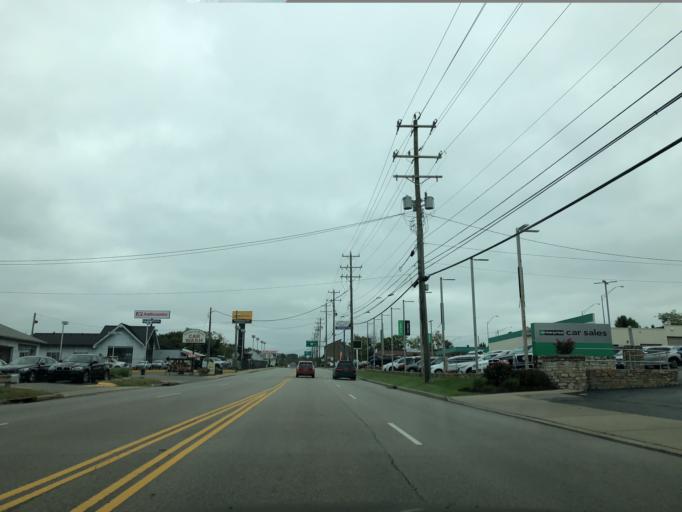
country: US
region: Ohio
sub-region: Hamilton County
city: Reading
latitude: 39.2120
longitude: -84.4542
